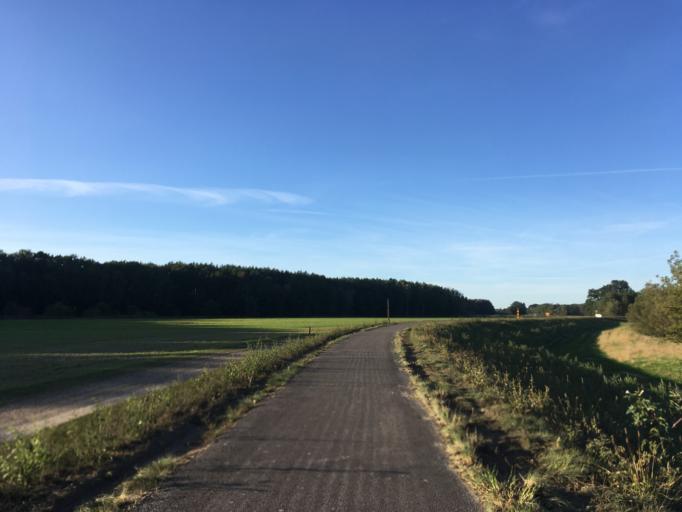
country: PL
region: Lubusz
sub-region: Powiat zarski
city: Trzebiel
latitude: 51.6515
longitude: 14.7505
